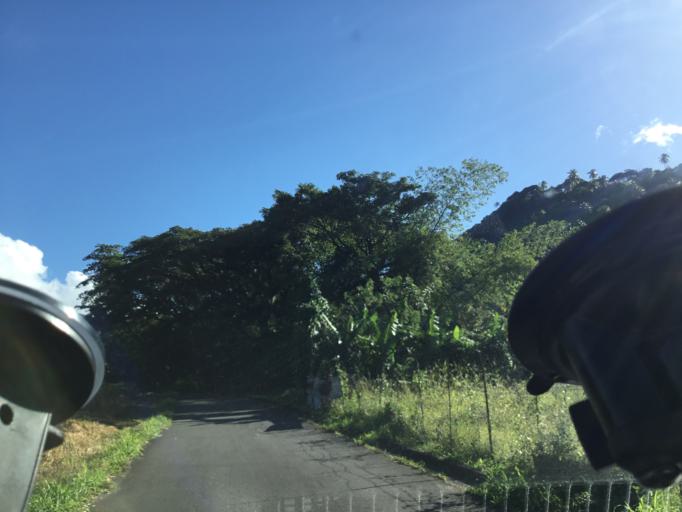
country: VC
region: Saint David
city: Chateaubelair
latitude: 13.3034
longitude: -61.2294
